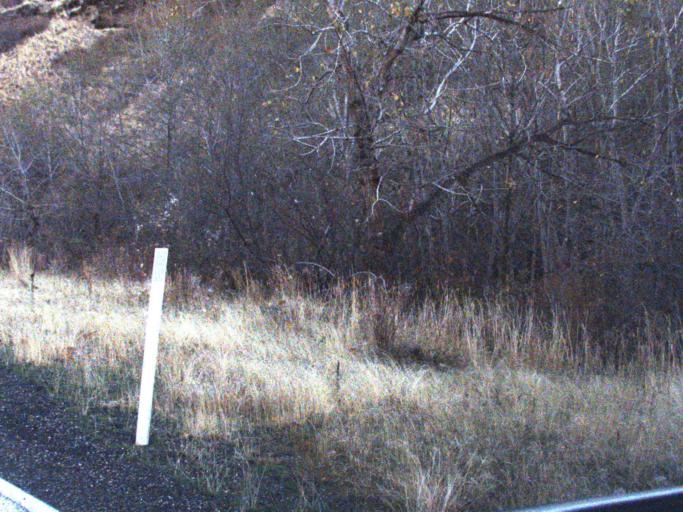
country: US
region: Washington
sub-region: Asotin County
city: Asotin
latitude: 46.0141
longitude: -117.2691
